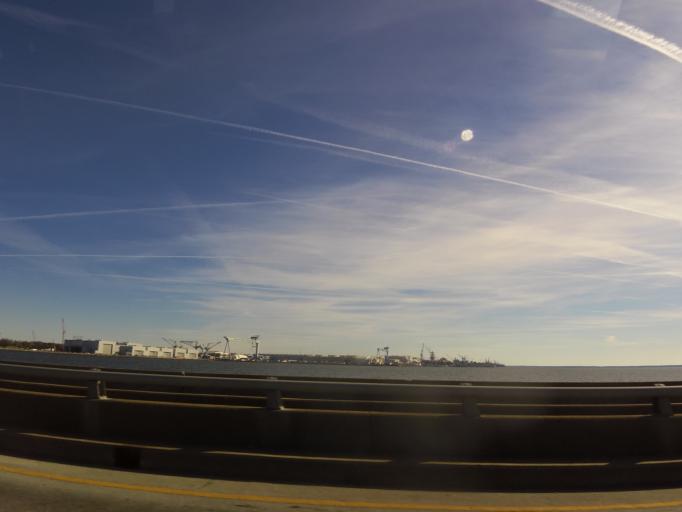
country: US
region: Virginia
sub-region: City of Newport News
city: Newport News
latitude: 37.0078
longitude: -76.4627
